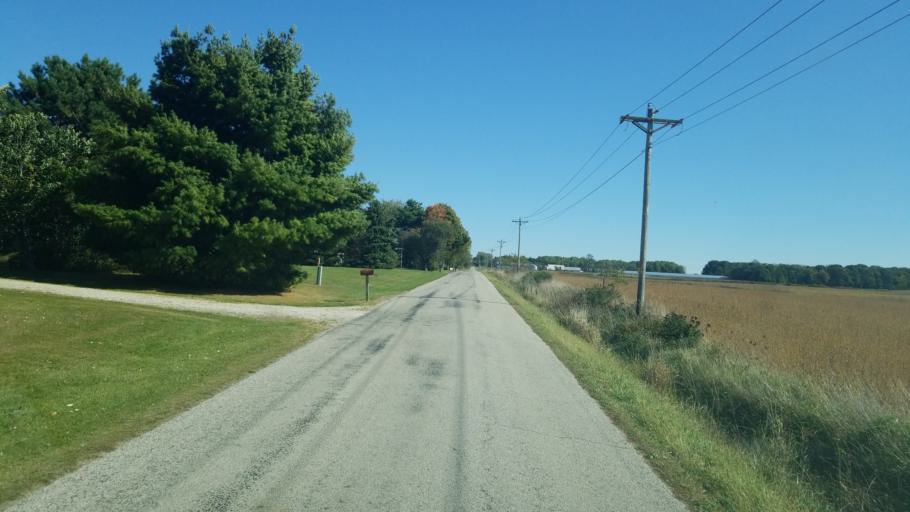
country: US
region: Ohio
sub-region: Huron County
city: Plymouth
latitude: 41.0454
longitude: -82.6265
